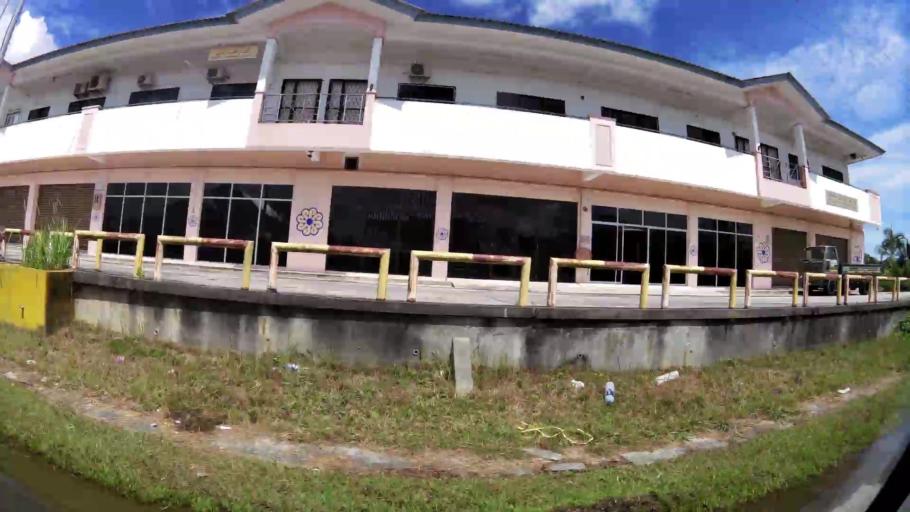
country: BN
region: Brunei and Muara
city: Bandar Seri Begawan
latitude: 4.9427
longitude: 114.9042
